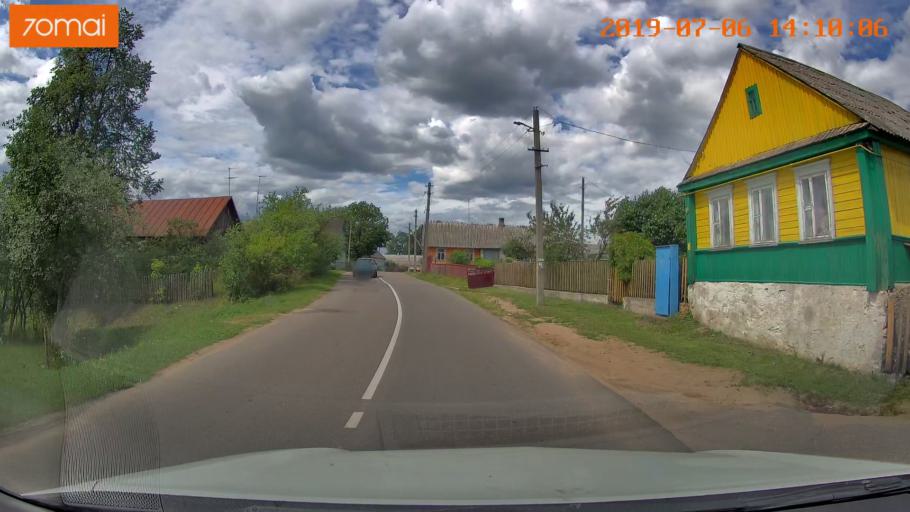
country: BY
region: Minsk
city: Ivyanyets
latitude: 53.8843
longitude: 26.7455
